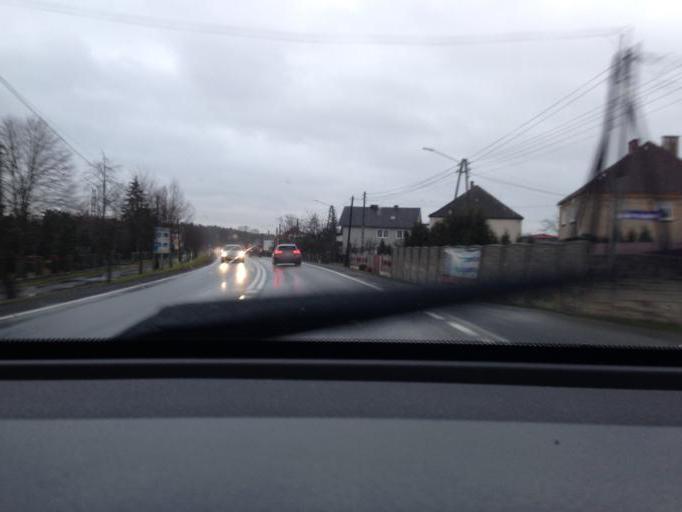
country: PL
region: Opole Voivodeship
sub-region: Powiat opolski
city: Wegry
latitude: 50.7107
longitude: 17.9882
